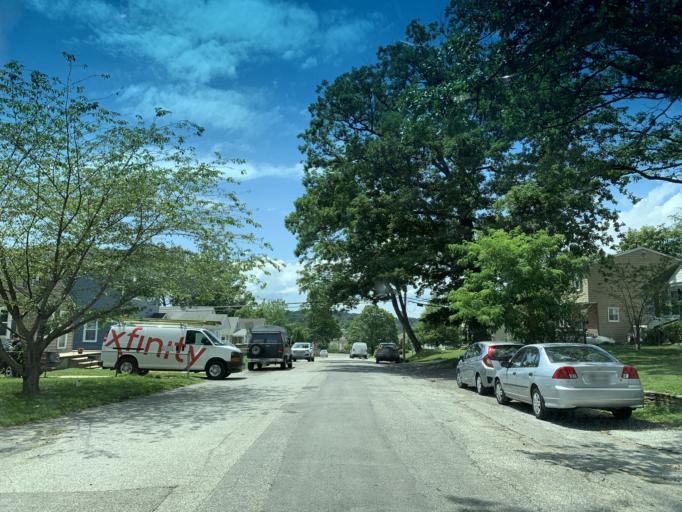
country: US
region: Maryland
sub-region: Baltimore County
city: Timonium
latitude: 39.4372
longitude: -76.6222
